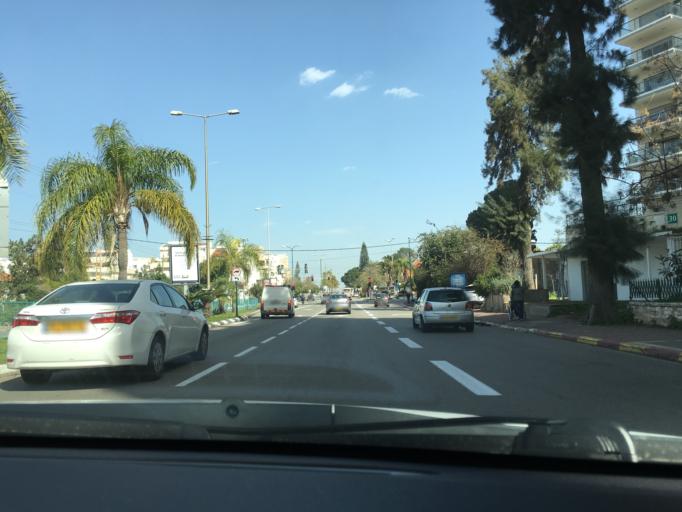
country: IL
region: Central District
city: Kfar Saba
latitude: 32.1777
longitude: 34.8941
